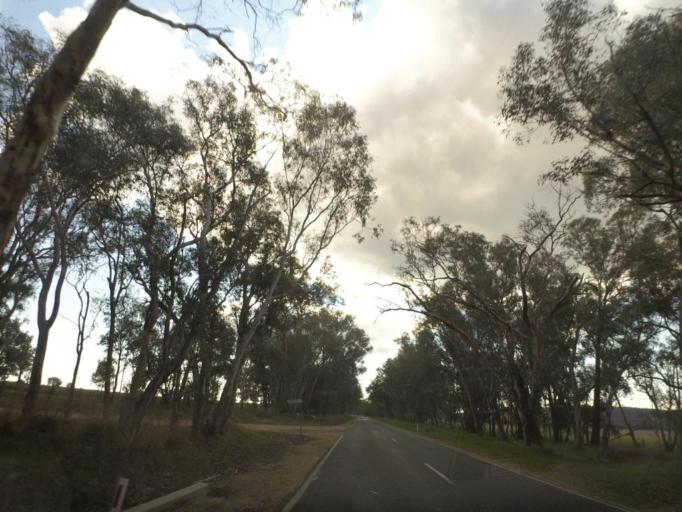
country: AU
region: New South Wales
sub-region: Corowa Shire
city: Howlong
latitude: -36.2019
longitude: 146.6207
